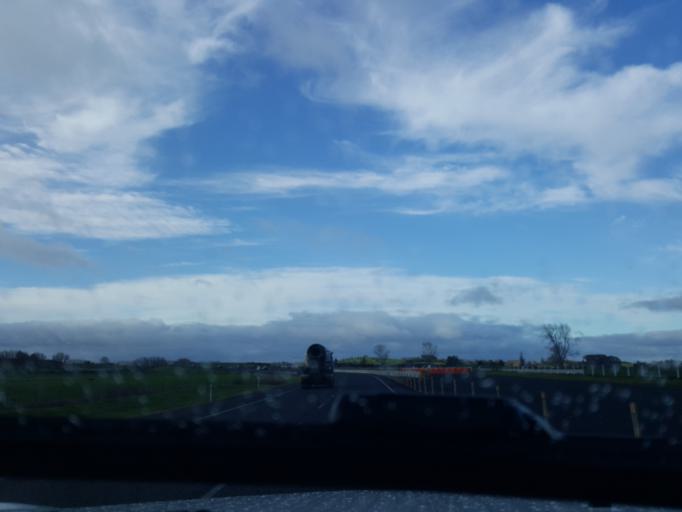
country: NZ
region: Waikato
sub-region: Waikato District
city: Ngaruawahia
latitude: -37.6750
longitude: 175.2094
